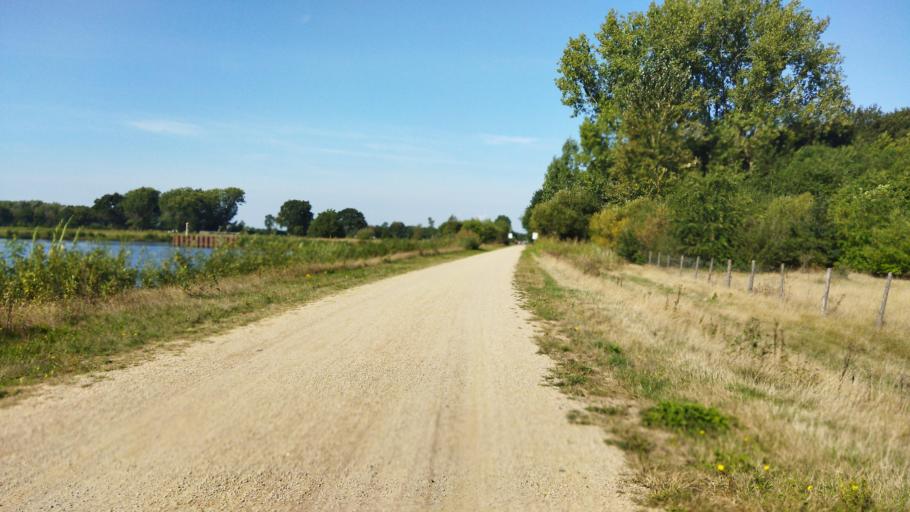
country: DE
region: Lower Saxony
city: Haren
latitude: 52.7781
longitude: 7.2632
